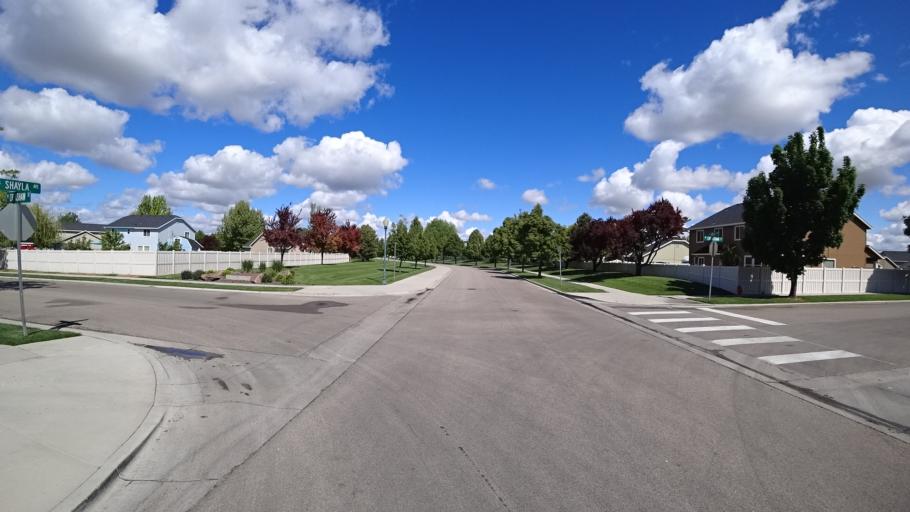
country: US
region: Idaho
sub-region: Ada County
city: Kuna
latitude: 43.5052
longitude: -116.4414
